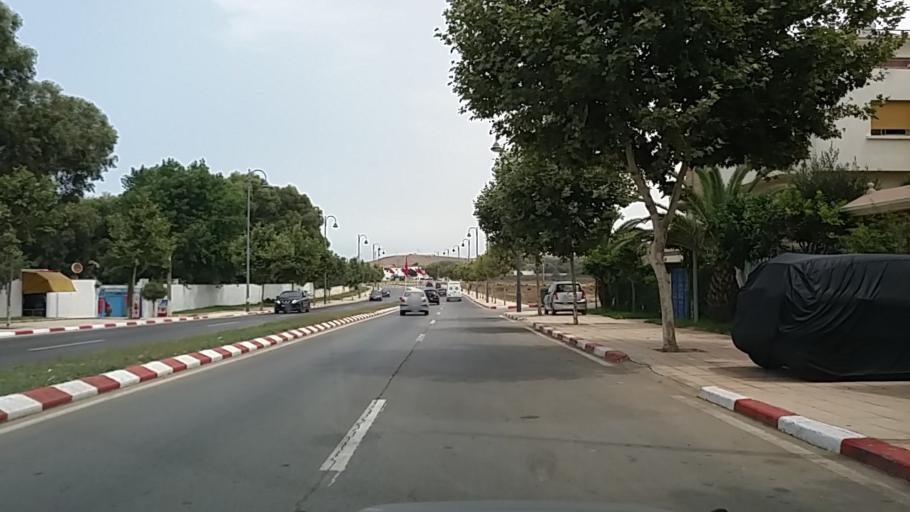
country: MA
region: Tanger-Tetouan
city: Asilah
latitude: 35.4717
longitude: -6.0282
